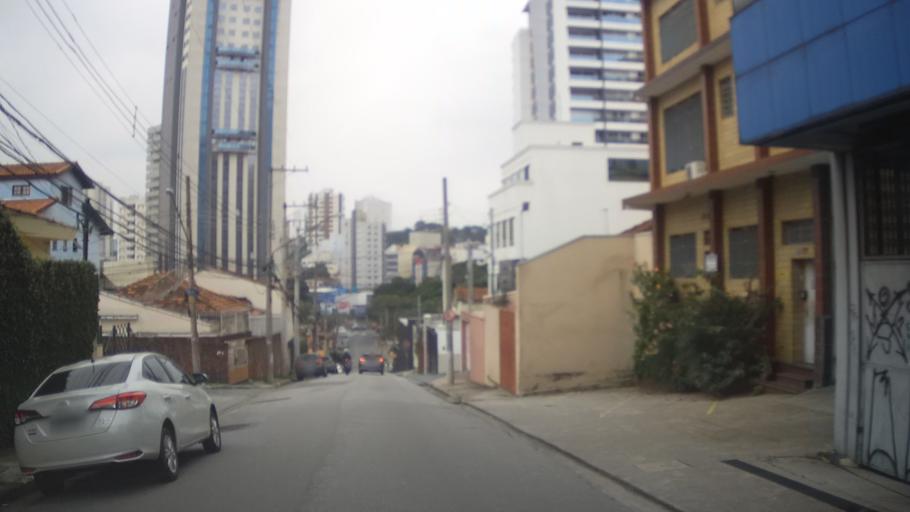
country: BR
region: Sao Paulo
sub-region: Guarulhos
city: Guarulhos
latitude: -23.4718
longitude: -46.5360
